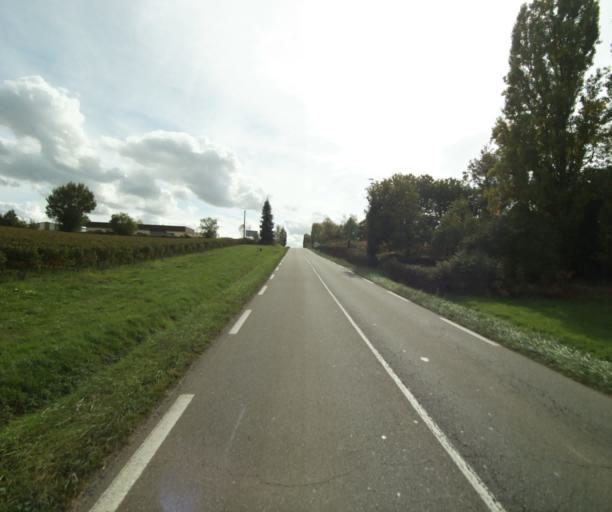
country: FR
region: Midi-Pyrenees
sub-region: Departement du Gers
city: Eauze
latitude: 43.8439
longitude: 0.0929
